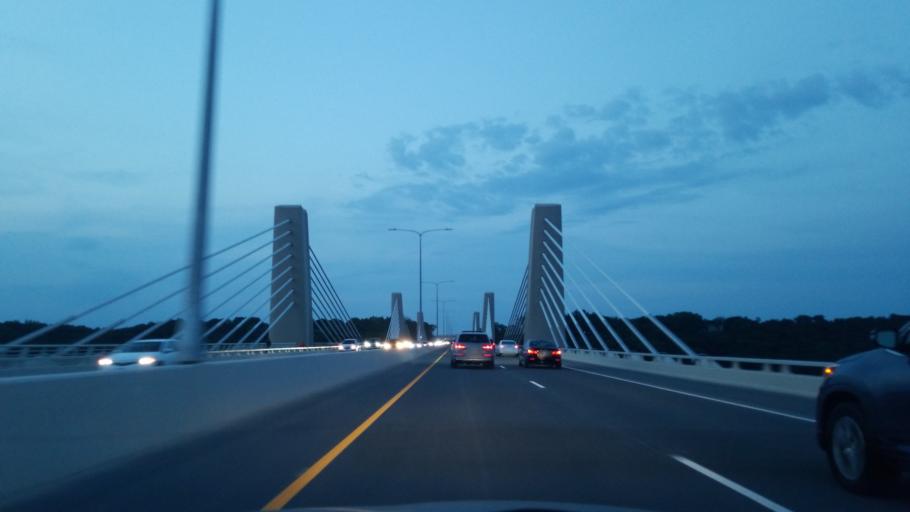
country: US
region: Minnesota
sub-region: Washington County
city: Oak Park Heights
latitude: 45.0414
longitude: -92.7855
